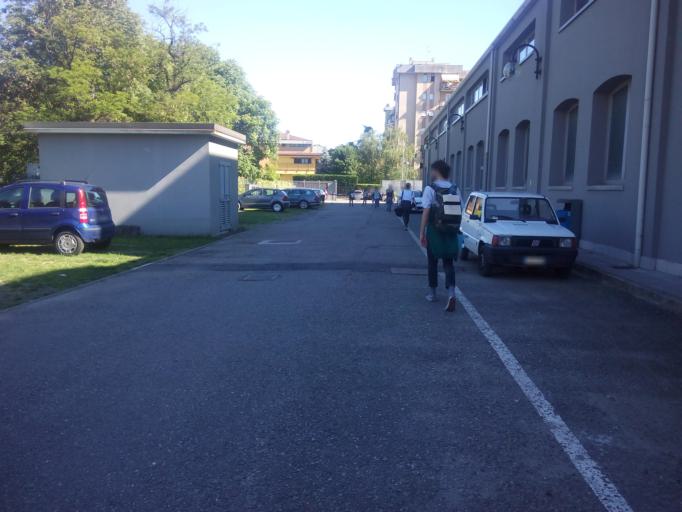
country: IT
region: Lombardy
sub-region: Citta metropolitana di Milano
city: Novate Milanese
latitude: 45.5049
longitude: 9.1665
